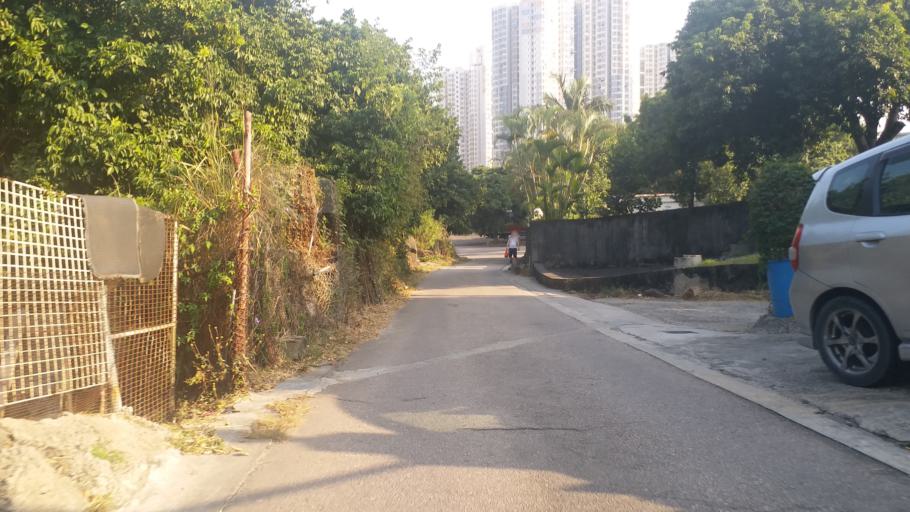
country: HK
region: Tuen Mun
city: Tuen Mun
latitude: 22.4175
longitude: 113.9733
